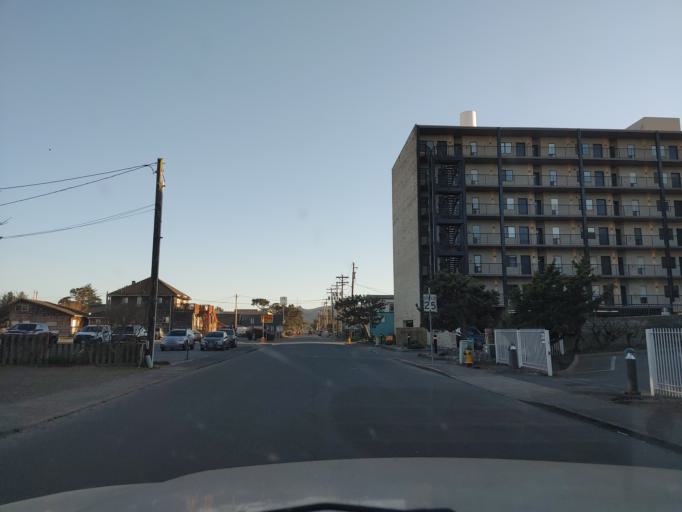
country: US
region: Oregon
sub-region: Clatsop County
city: Seaside
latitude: 45.9917
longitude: -123.9294
